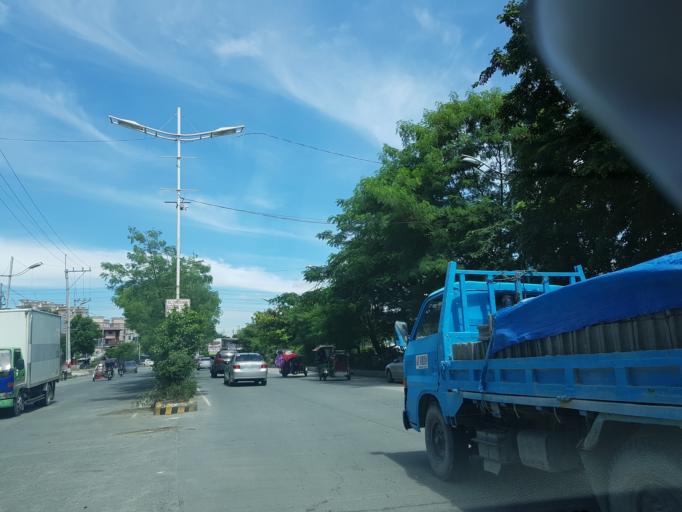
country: PH
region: Calabarzon
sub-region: Province of Rizal
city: Pateros
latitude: 14.5299
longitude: 121.0605
